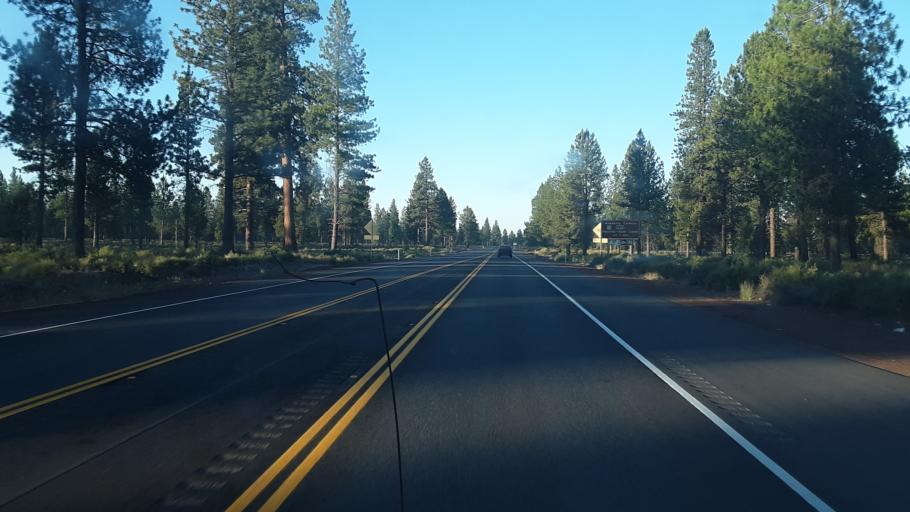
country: US
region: Oregon
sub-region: Deschutes County
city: Three Rivers
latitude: 43.7668
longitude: -121.4533
